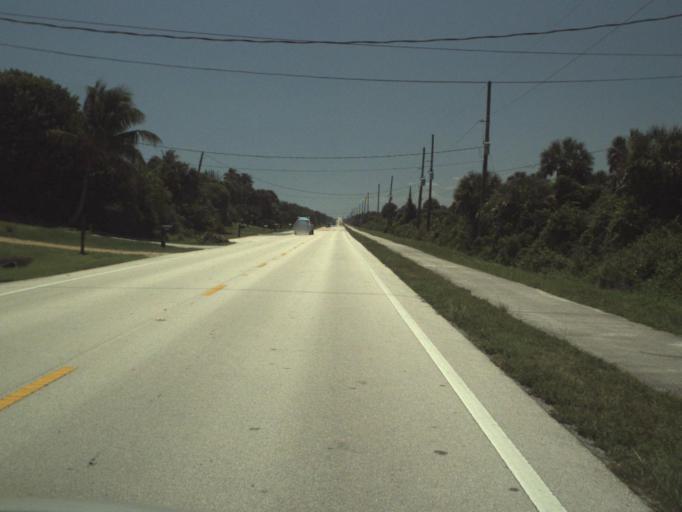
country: US
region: Florida
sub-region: Brevard County
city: Micco
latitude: 27.8798
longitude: -80.4585
